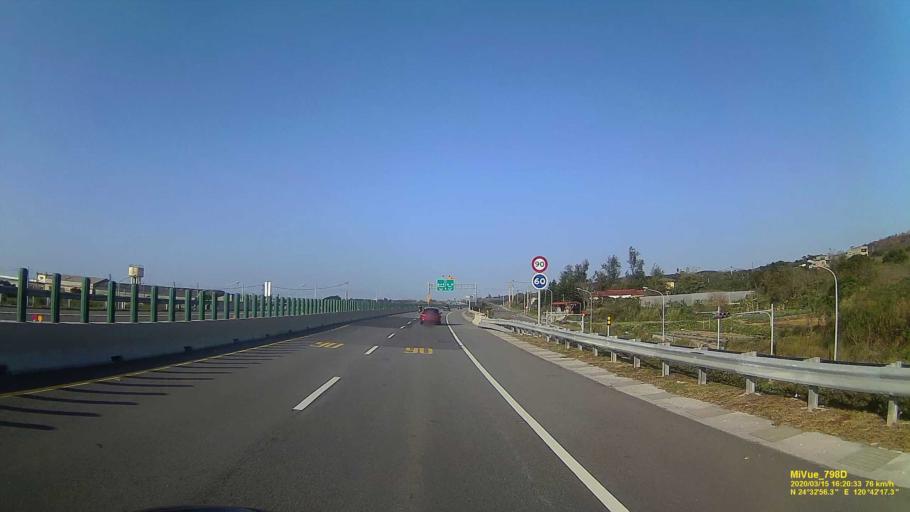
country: TW
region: Taiwan
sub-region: Miaoli
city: Miaoli
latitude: 24.5487
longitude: 120.7048
